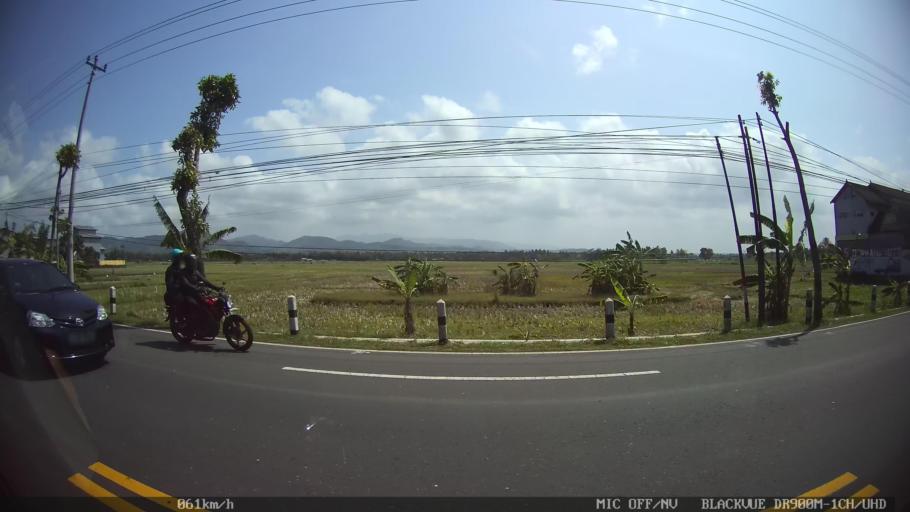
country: ID
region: Daerah Istimewa Yogyakarta
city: Srandakan
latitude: -7.8911
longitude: 110.1219
